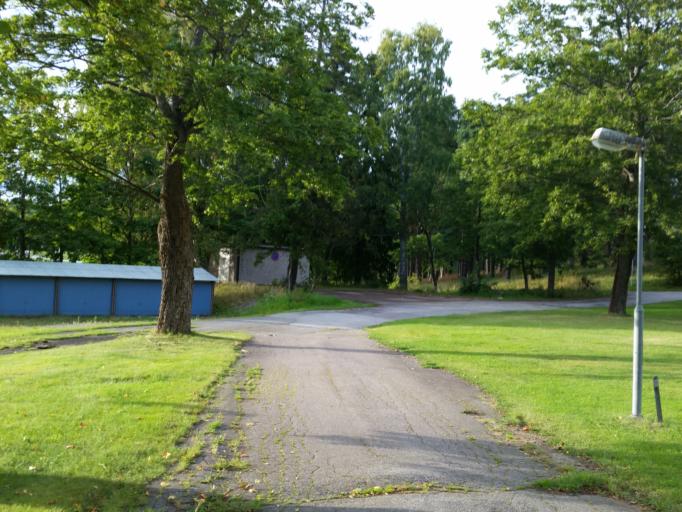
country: SE
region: Stockholm
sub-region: Upplands Vasby Kommun
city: Upplands Vaesby
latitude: 59.5401
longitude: 17.9132
